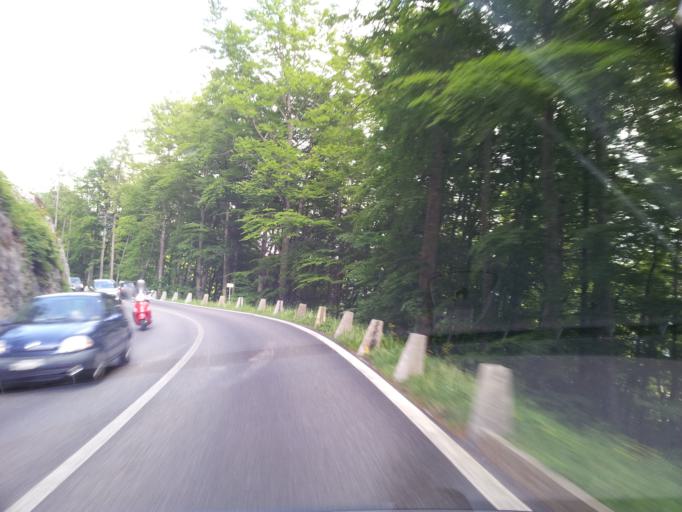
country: CH
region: Obwalden
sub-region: Obwalden
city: Lungern
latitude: 46.7505
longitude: 8.1234
